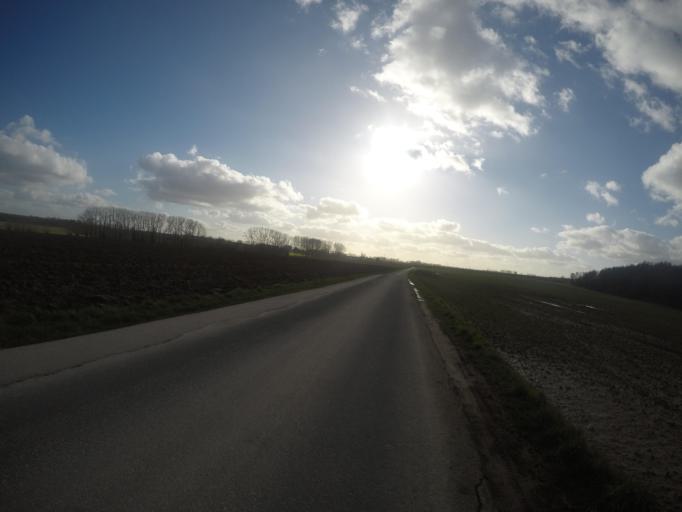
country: BE
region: Wallonia
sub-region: Province du Brabant Wallon
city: Rebecq-Rognon
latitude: 50.6837
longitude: 4.1153
